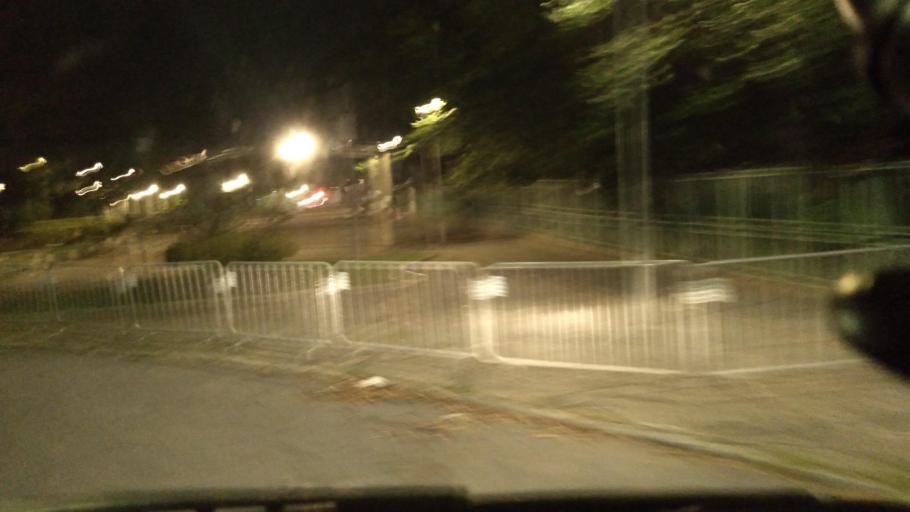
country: BR
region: Minas Gerais
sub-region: Belo Horizonte
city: Belo Horizonte
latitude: -19.9158
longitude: -43.9169
